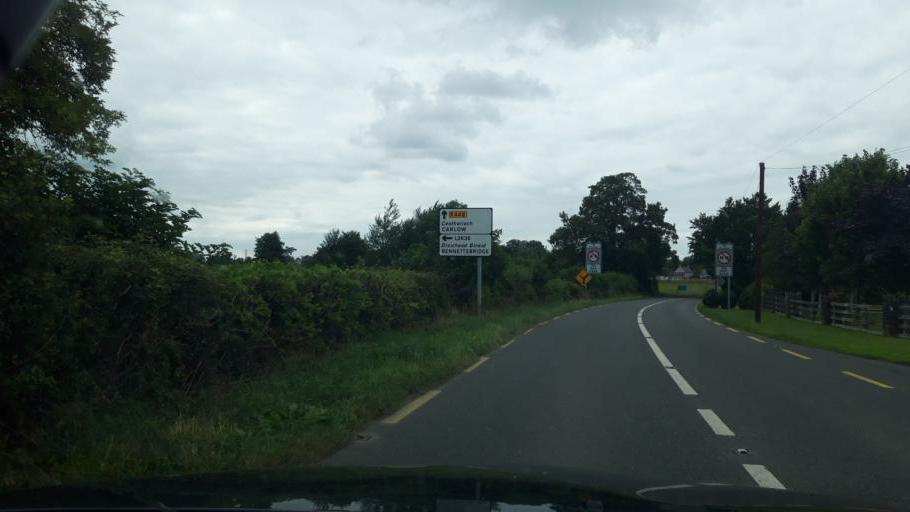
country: IE
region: Leinster
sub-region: Kilkenny
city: Thomastown
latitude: 52.6250
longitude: -7.0717
